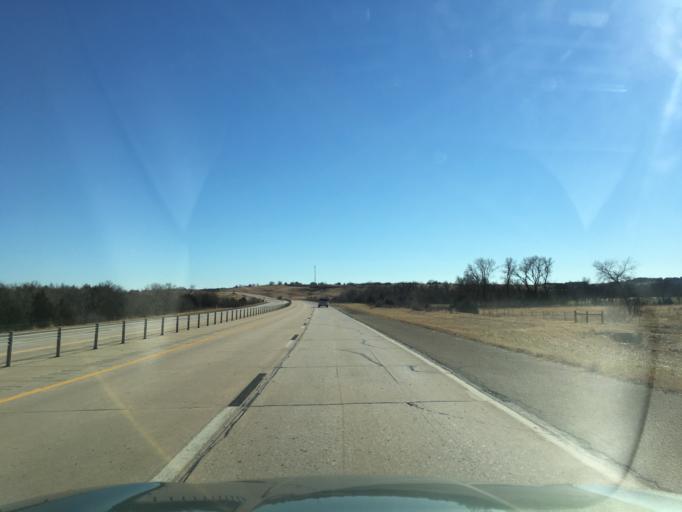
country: US
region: Oklahoma
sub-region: Payne County
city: Stillwater
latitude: 36.2566
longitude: -96.9710
